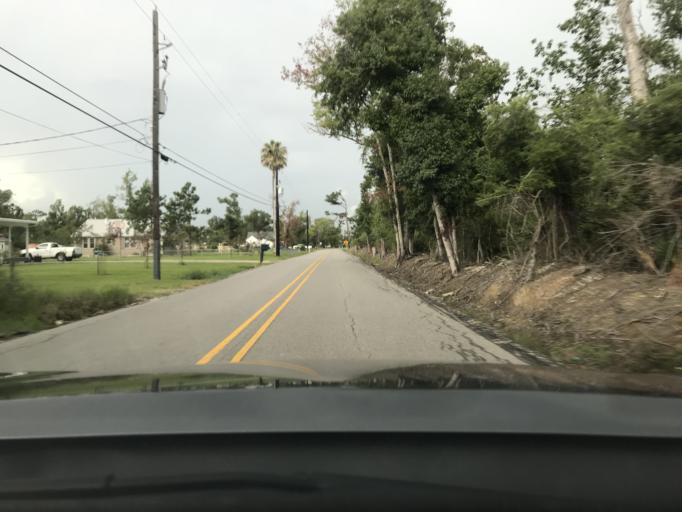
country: US
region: Louisiana
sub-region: Calcasieu Parish
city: Westlake
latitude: 30.2571
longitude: -93.2425
